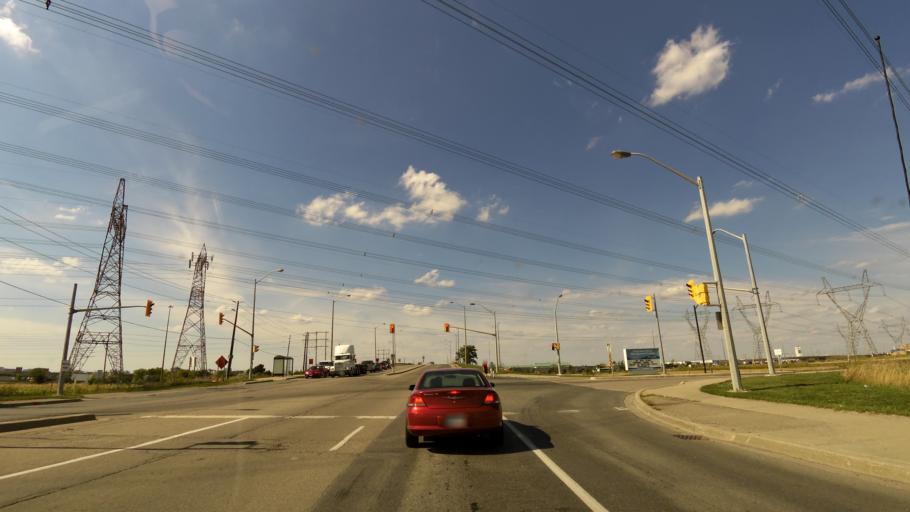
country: CA
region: Ontario
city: Brampton
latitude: 43.7100
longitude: -79.6738
